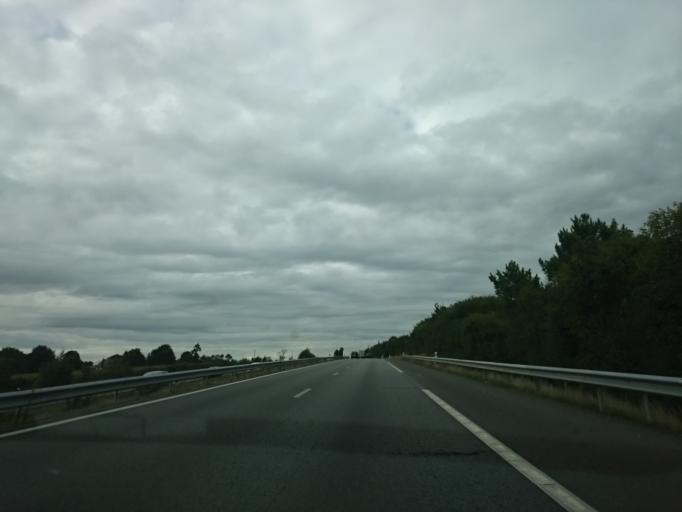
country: FR
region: Brittany
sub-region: Departement d'Ille-et-Vilaine
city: Crevin
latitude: 47.9432
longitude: -1.6762
